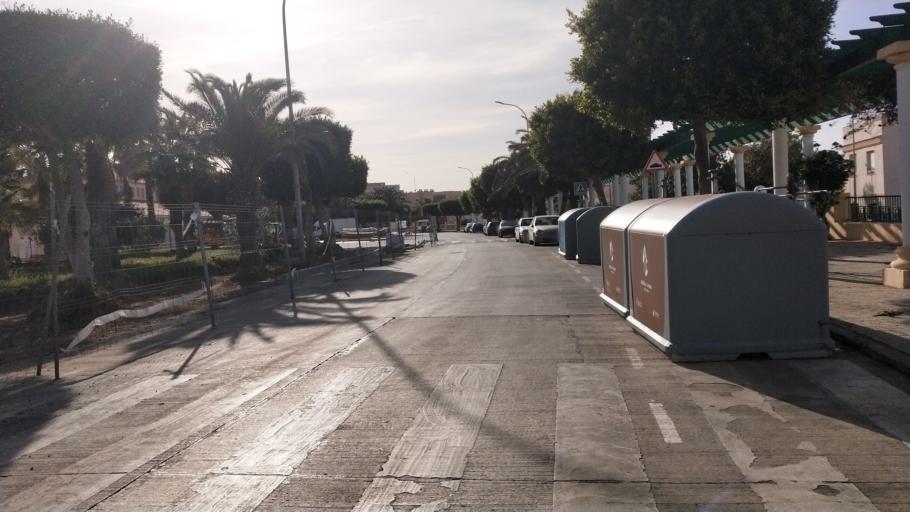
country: ES
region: Melilla
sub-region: Melilla
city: Melilla
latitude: 35.2886
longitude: -2.9496
